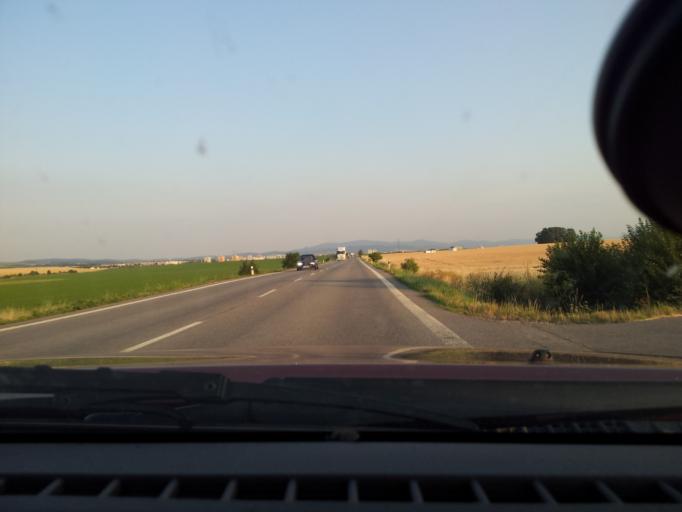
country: SK
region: Trnavsky
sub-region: Okres Senica
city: Senica
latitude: 48.7106
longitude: 17.3615
